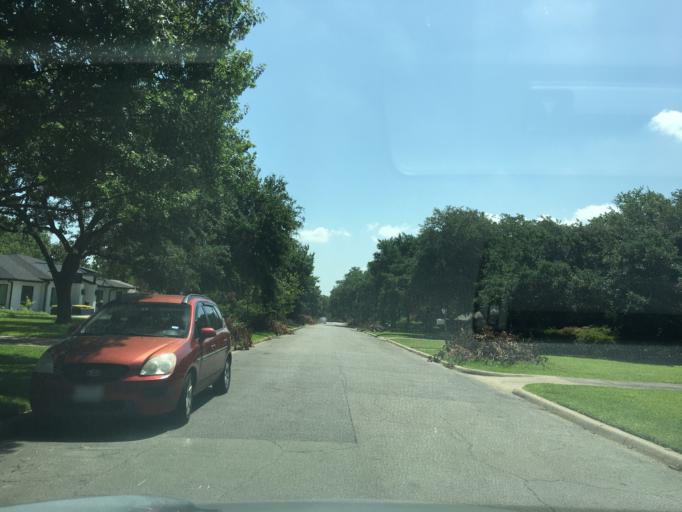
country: US
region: Texas
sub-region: Dallas County
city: University Park
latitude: 32.8990
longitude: -96.7823
